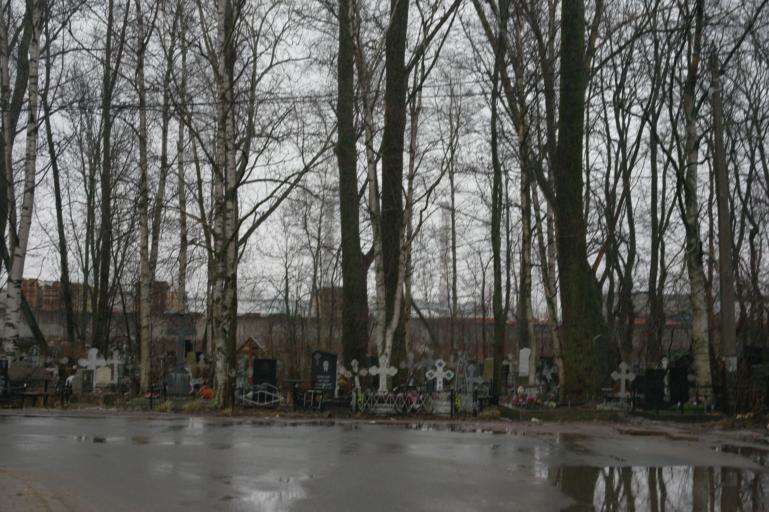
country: RU
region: St.-Petersburg
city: Komendantsky aerodrom
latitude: 59.9942
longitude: 30.2694
